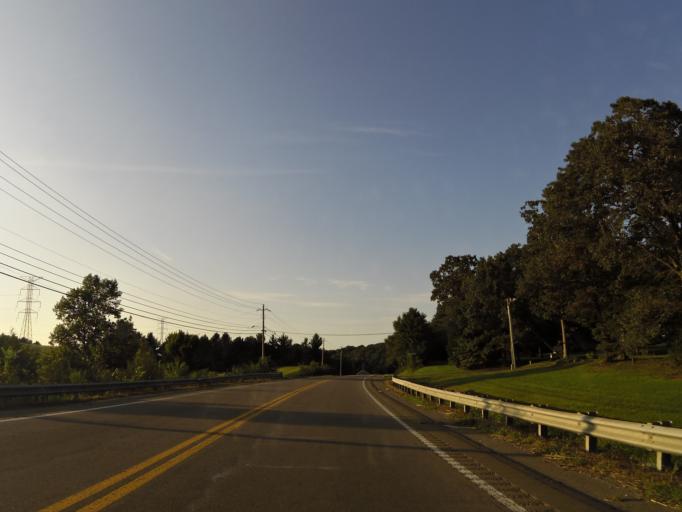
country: US
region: Tennessee
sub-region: McMinn County
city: Athens
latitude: 35.4901
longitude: -84.6003
